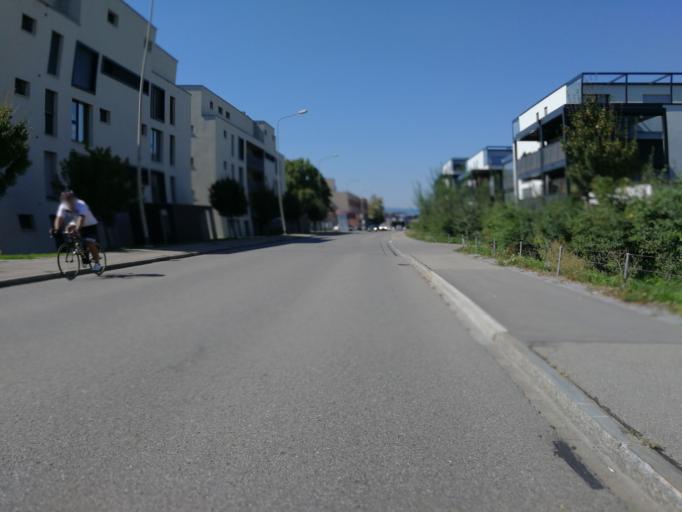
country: CH
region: Zurich
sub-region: Bezirk Hinwil
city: Hinwil
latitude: 47.3035
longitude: 8.8379
